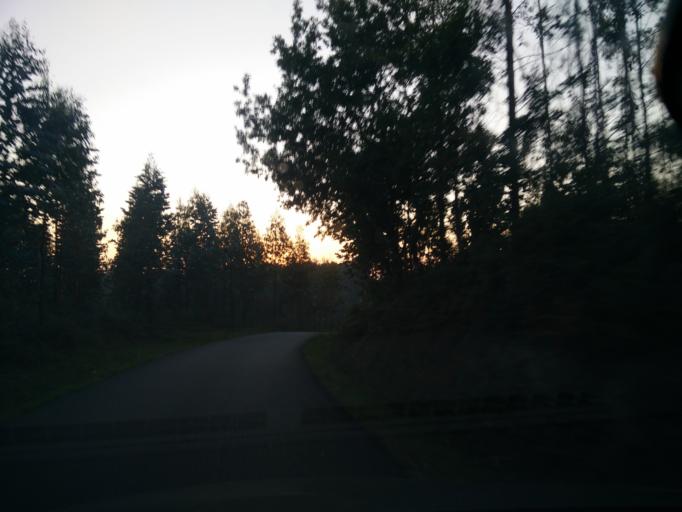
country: ES
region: Galicia
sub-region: Provincia da Coruna
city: Monfero
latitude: 43.3528
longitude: -8.0565
